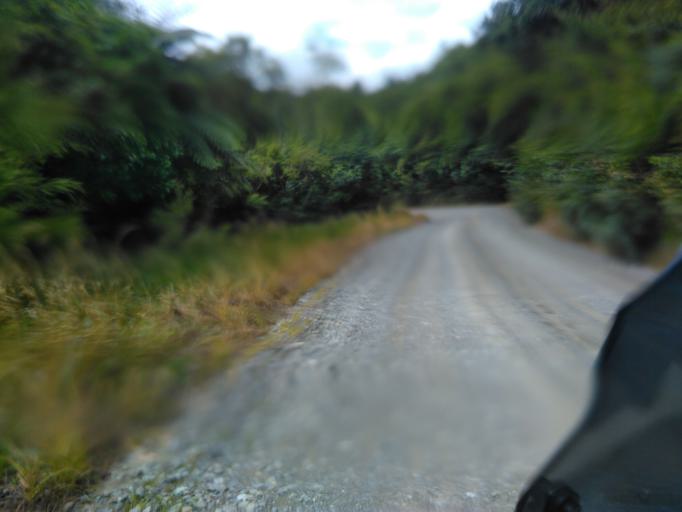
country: NZ
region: Gisborne
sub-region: Gisborne District
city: Gisborne
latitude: -38.1766
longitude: 178.1337
